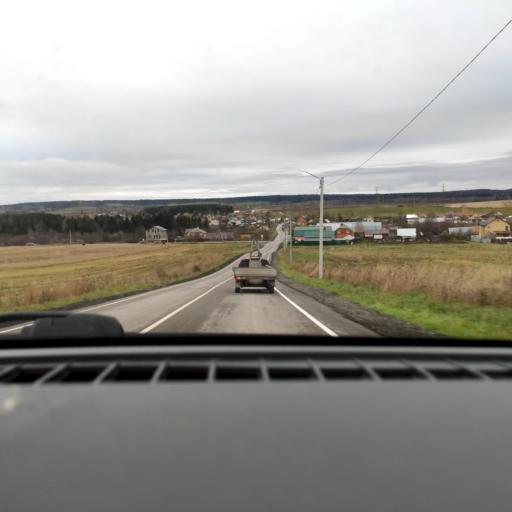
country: RU
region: Perm
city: Ferma
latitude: 57.9208
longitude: 56.3223
